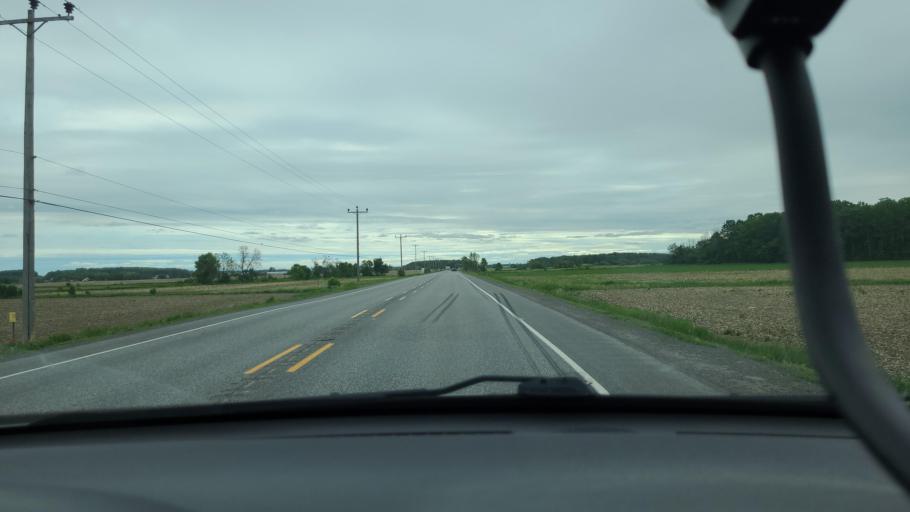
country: CA
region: Quebec
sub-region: Lanaudiere
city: Saint-Jacques
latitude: 45.9157
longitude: -73.6418
